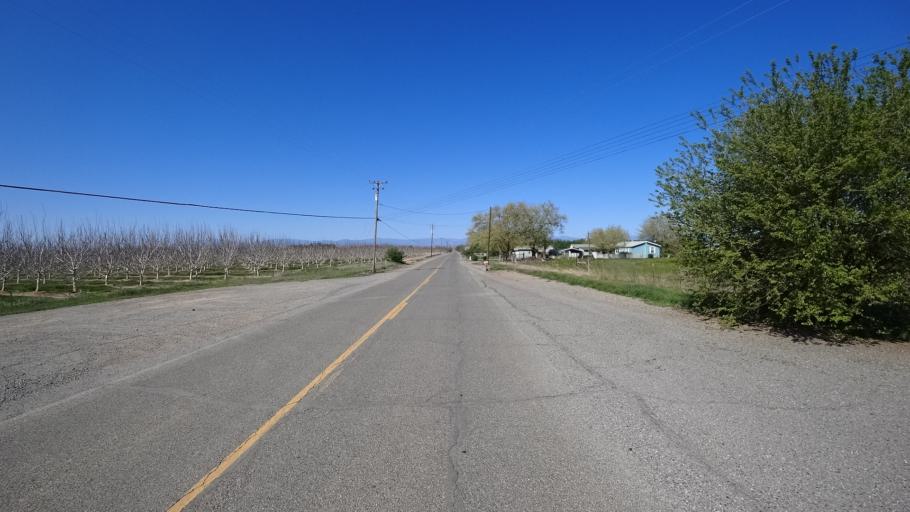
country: US
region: California
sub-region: Glenn County
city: Orland
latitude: 39.6971
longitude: -122.2075
